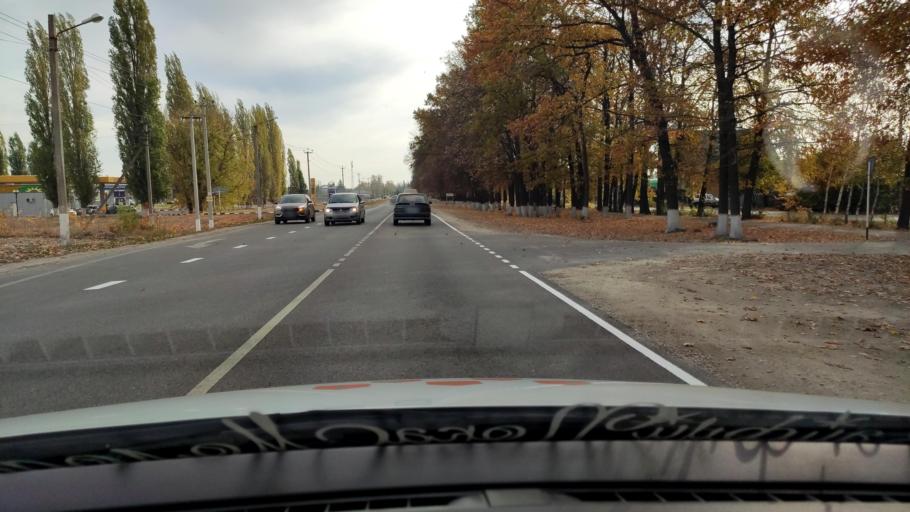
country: RU
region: Voronezj
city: Ramon'
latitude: 51.9129
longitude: 39.3197
